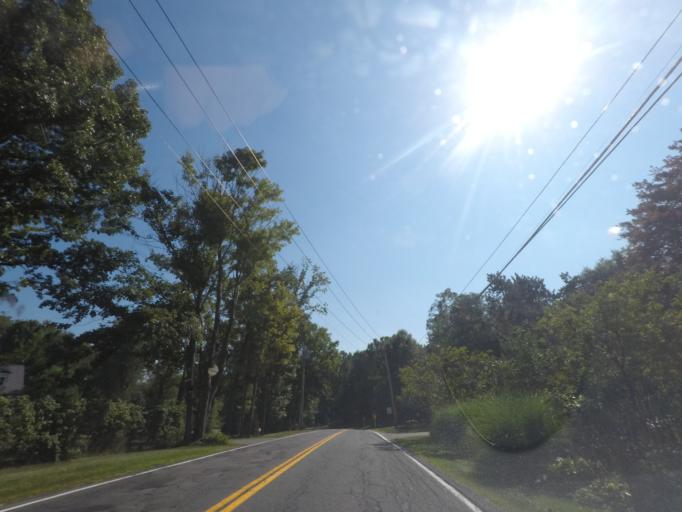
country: US
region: New York
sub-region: Albany County
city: Menands
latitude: 42.7115
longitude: -73.7428
